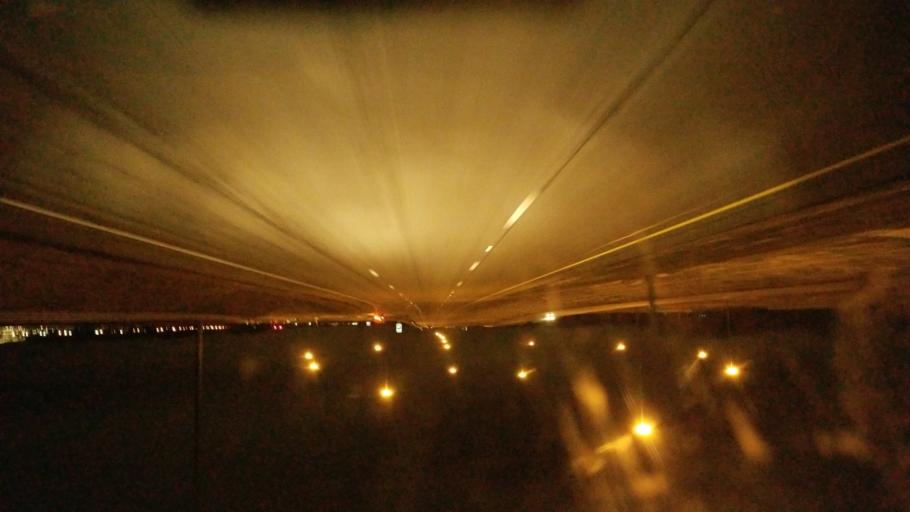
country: US
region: Ohio
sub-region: Franklin County
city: New Albany
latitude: 40.0808
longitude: -82.7474
